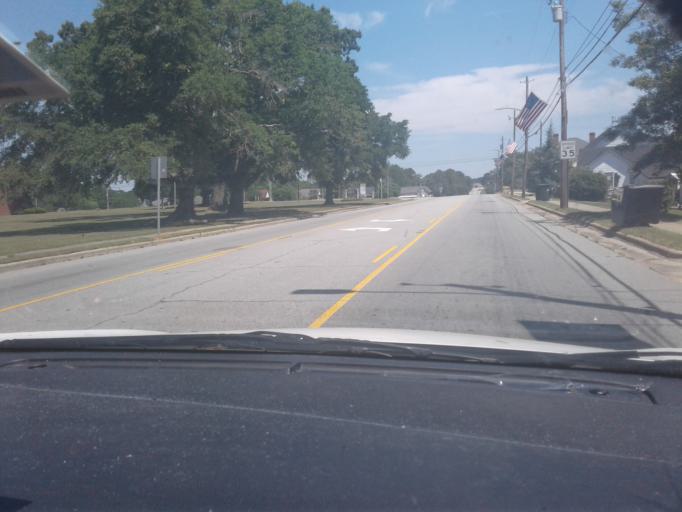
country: US
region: North Carolina
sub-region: Harnett County
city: Erwin
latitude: 35.3286
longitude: -78.6760
